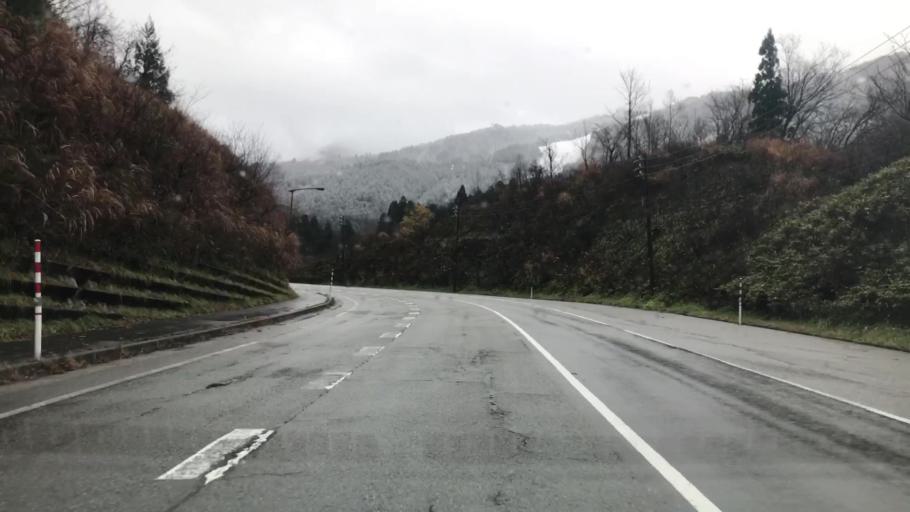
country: JP
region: Toyama
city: Kamiichi
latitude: 36.5780
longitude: 137.4089
